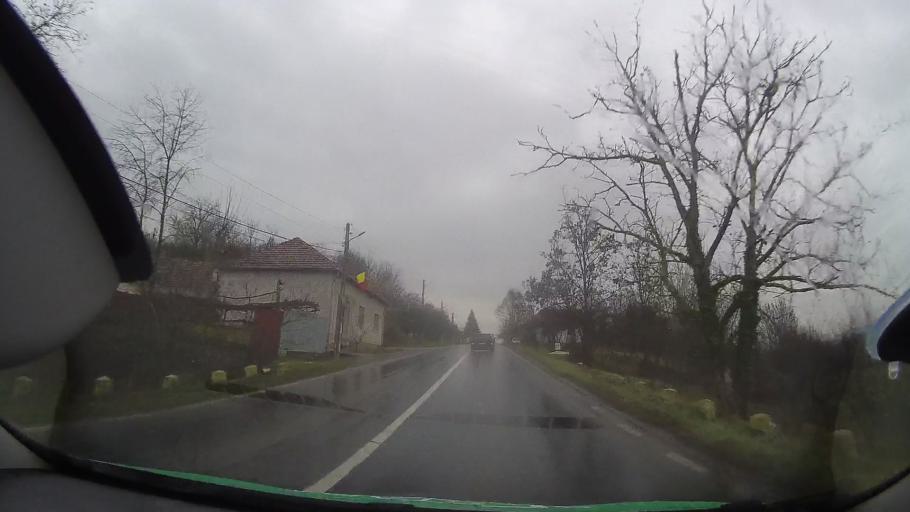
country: RO
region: Bihor
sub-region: Comuna Rabagani
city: Rabagani
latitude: 46.7604
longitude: 22.1934
